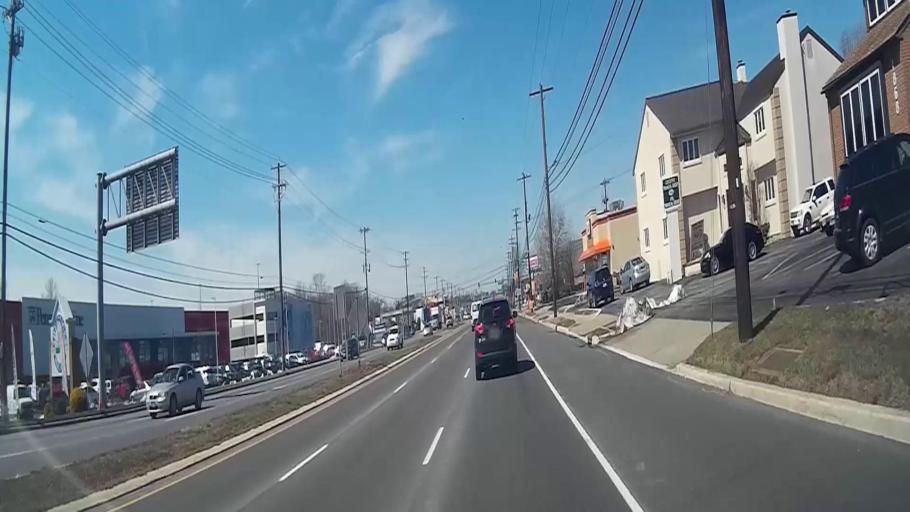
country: US
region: New Jersey
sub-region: Camden County
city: Springdale
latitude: 39.9043
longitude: -74.9704
